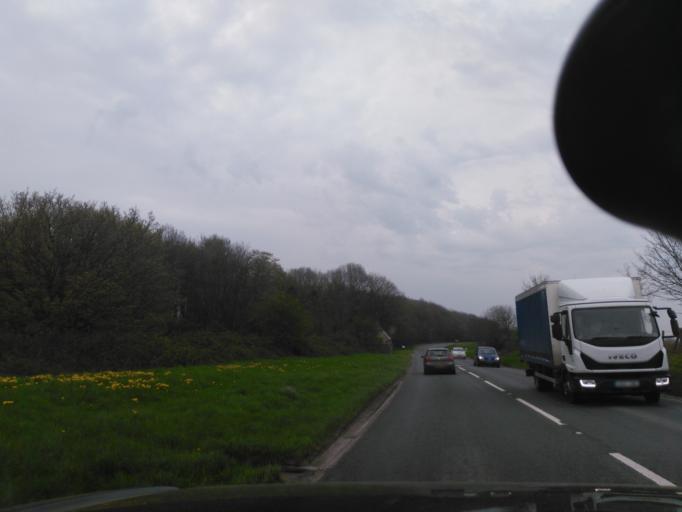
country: GB
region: England
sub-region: Somerset
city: Frome
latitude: 51.2081
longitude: -2.3484
